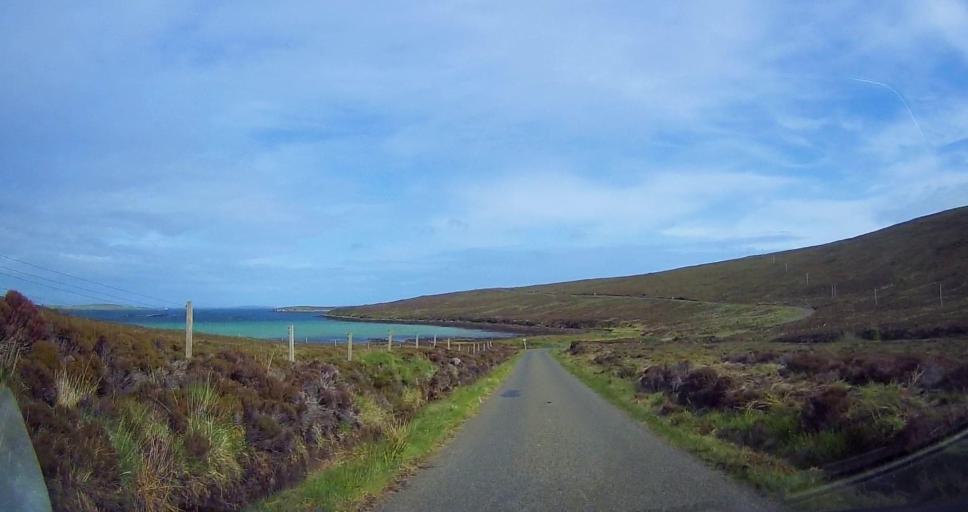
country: GB
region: Scotland
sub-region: Orkney Islands
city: Stromness
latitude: 58.8712
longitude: -3.2341
